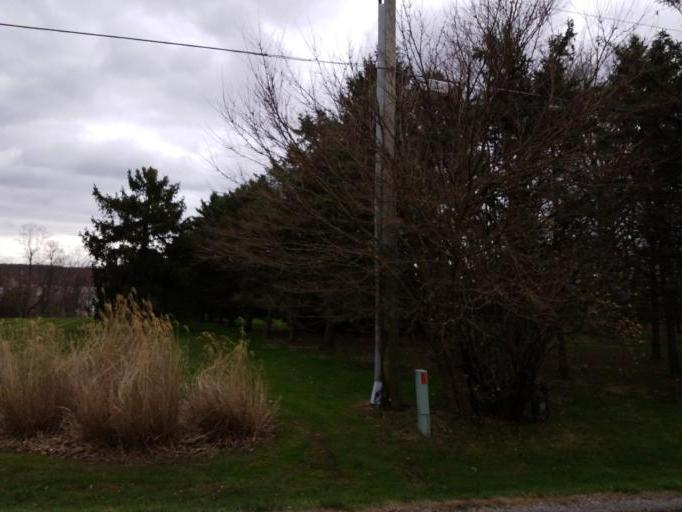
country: US
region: Ohio
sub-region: Franklin County
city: Westerville
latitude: 40.1560
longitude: -82.8803
